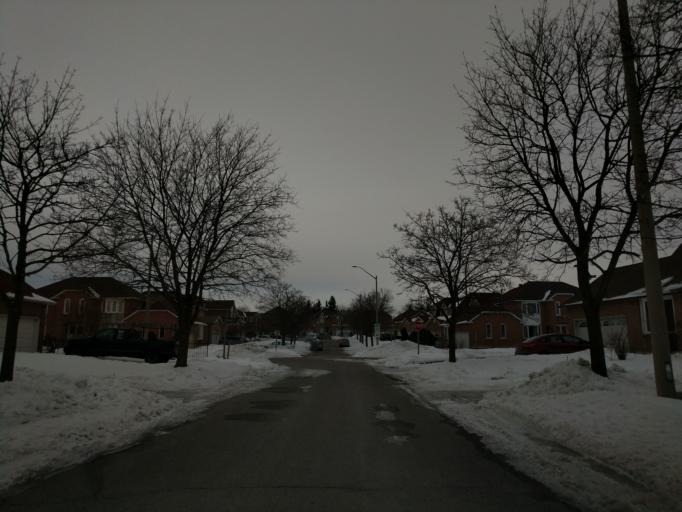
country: CA
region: Ontario
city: Markham
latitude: 43.8435
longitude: -79.2728
